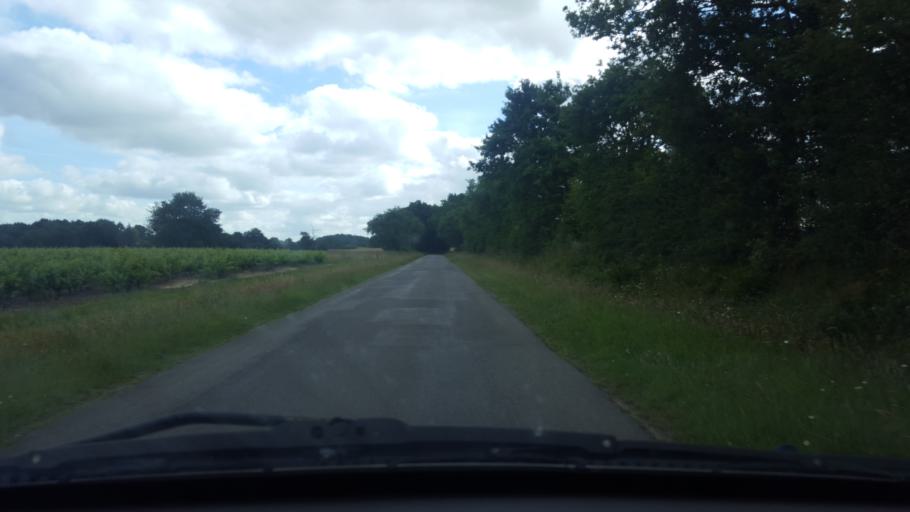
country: FR
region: Pays de la Loire
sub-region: Departement de la Loire-Atlantique
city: Saint-Philbert-de-Grand-Lieu
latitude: 47.0126
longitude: -1.6731
